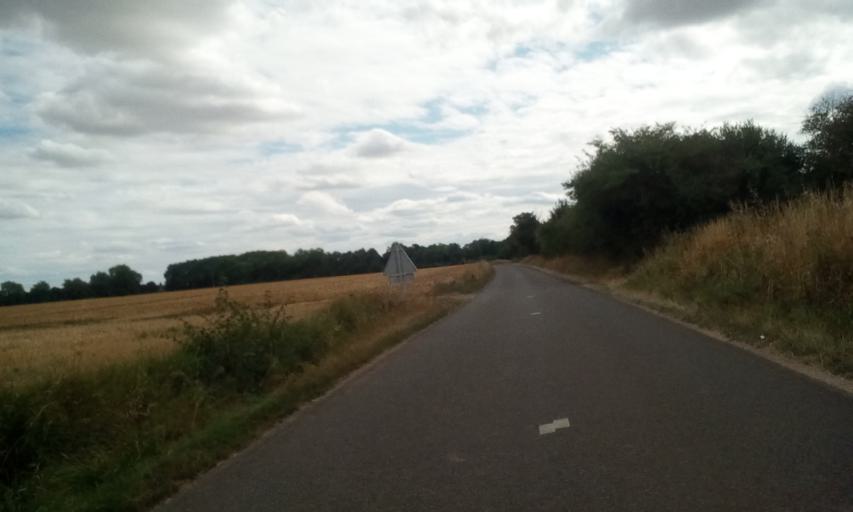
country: FR
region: Lower Normandy
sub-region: Departement du Calvados
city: Bellengreville
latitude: 49.1316
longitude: -0.2032
